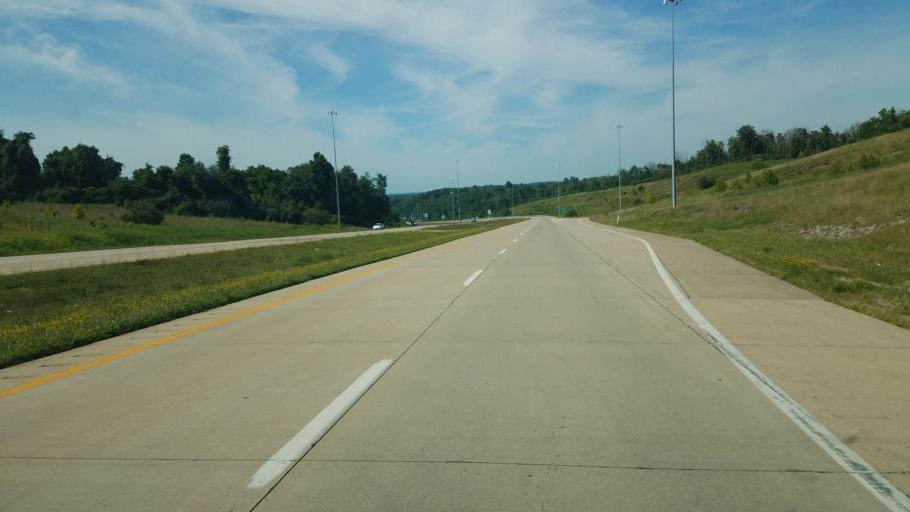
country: US
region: Ohio
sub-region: Athens County
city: Athens
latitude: 39.2954
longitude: -82.1032
